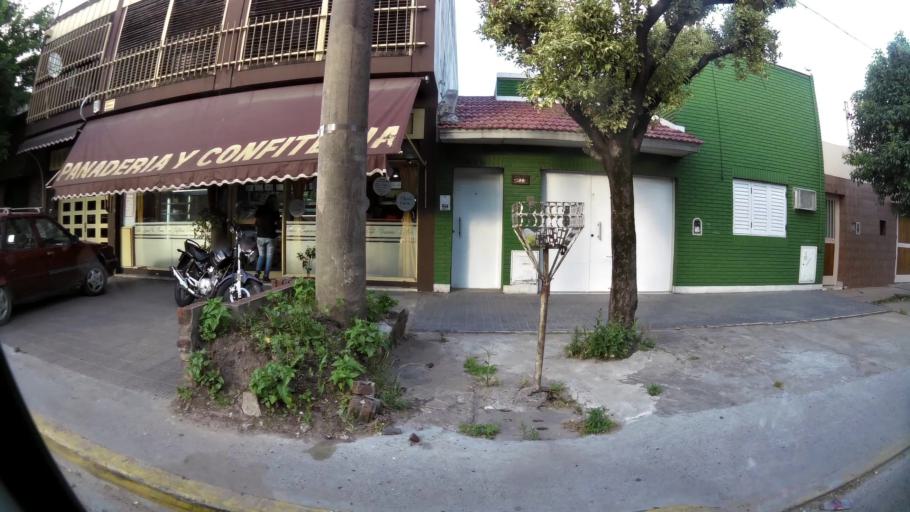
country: AR
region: Buenos Aires
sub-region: Partido de La Plata
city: La Plata
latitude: -34.8924
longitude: -57.9469
